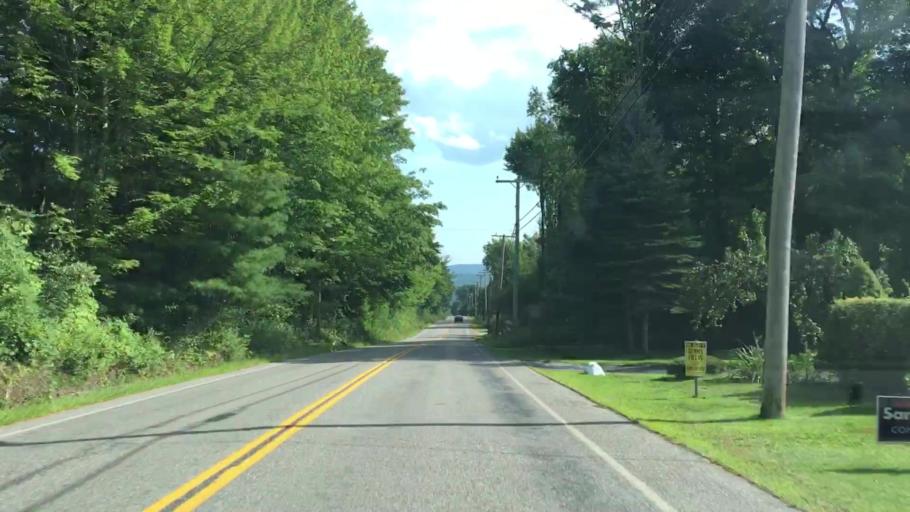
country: US
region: New Hampshire
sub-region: Belknap County
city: Sanbornton
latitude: 43.4730
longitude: -71.5700
